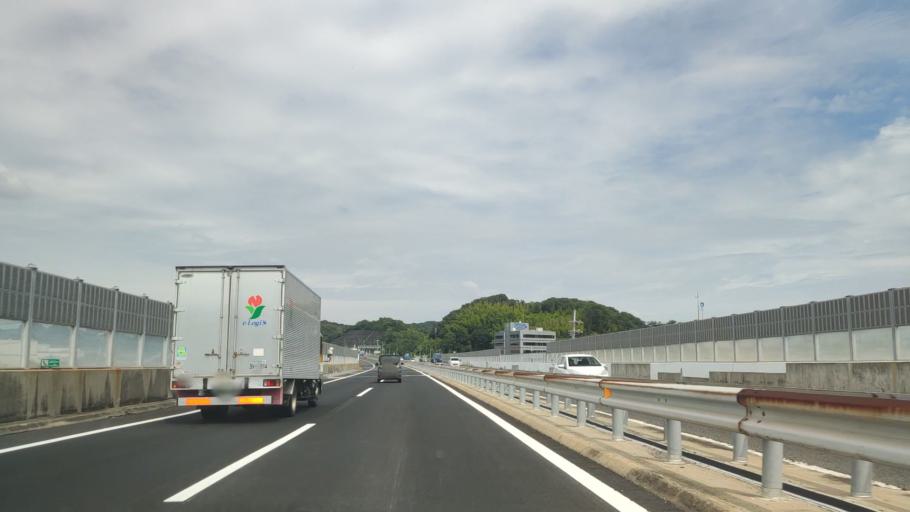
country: JP
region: Wakayama
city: Kainan
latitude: 34.1525
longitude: 135.2292
